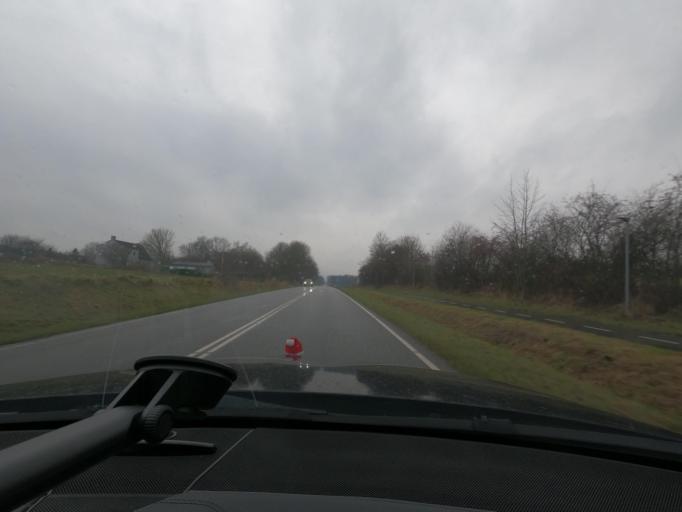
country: DK
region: South Denmark
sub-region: Sonderborg Kommune
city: Sonderborg
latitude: 54.9063
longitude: 9.8492
